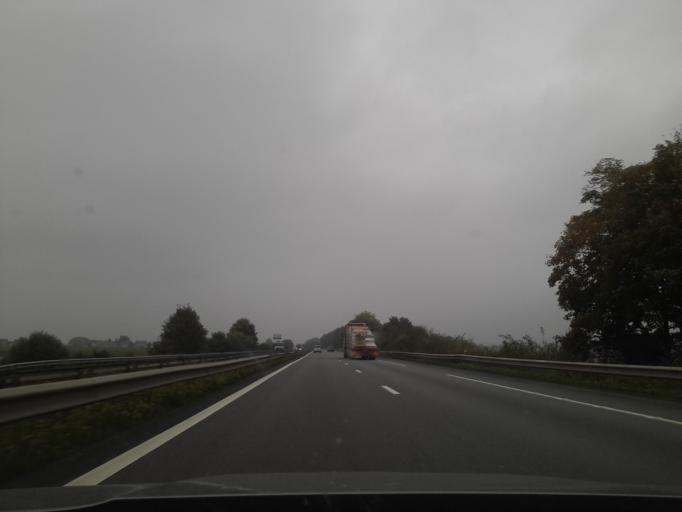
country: FR
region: Nord-Pas-de-Calais
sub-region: Departement du Nord
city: Lieu-Saint-Amand
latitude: 50.2833
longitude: 3.3485
